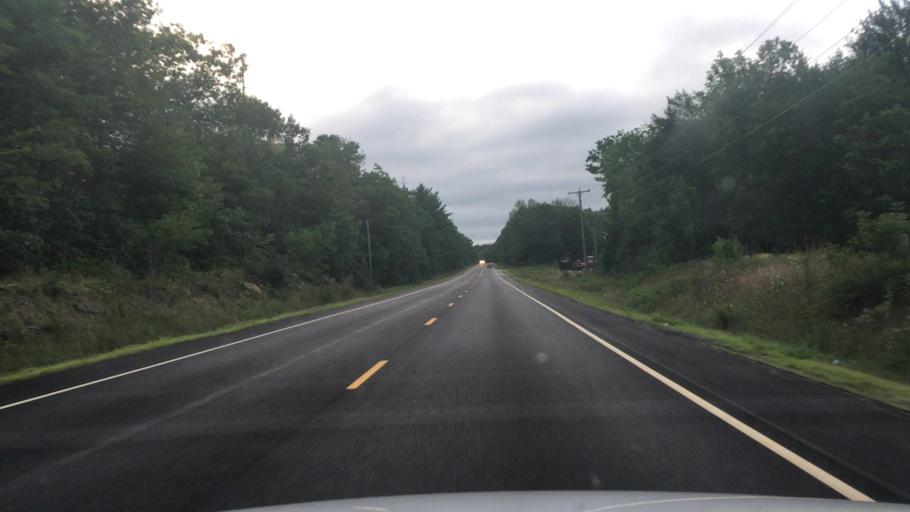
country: US
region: Maine
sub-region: Waldo County
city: Searsmont
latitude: 44.4041
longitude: -69.1671
